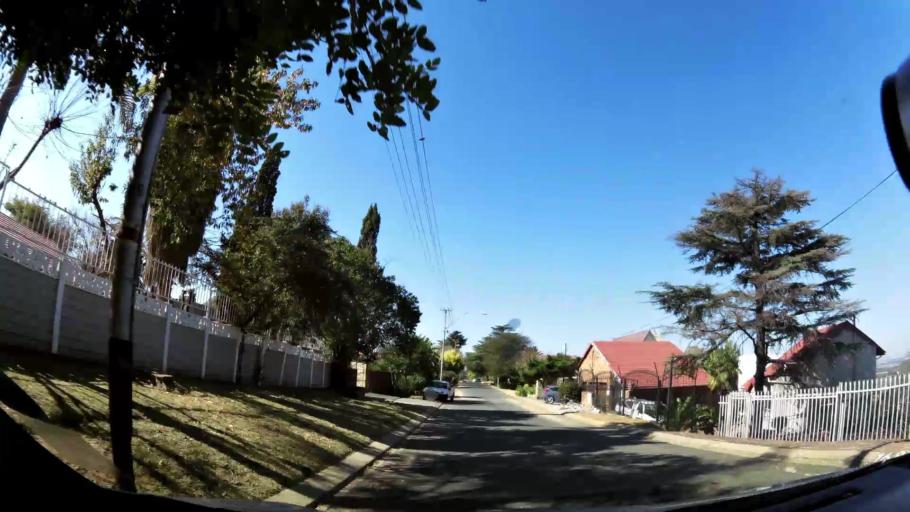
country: ZA
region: Gauteng
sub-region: City of Johannesburg Metropolitan Municipality
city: Johannesburg
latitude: -26.2685
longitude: 28.0006
